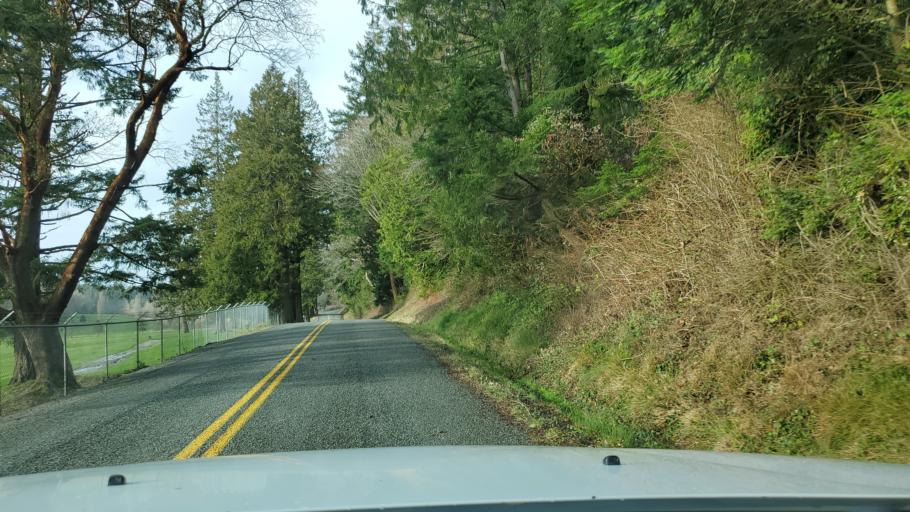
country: US
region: Washington
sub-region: Skagit County
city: Anacortes
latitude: 48.4506
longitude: -122.5741
